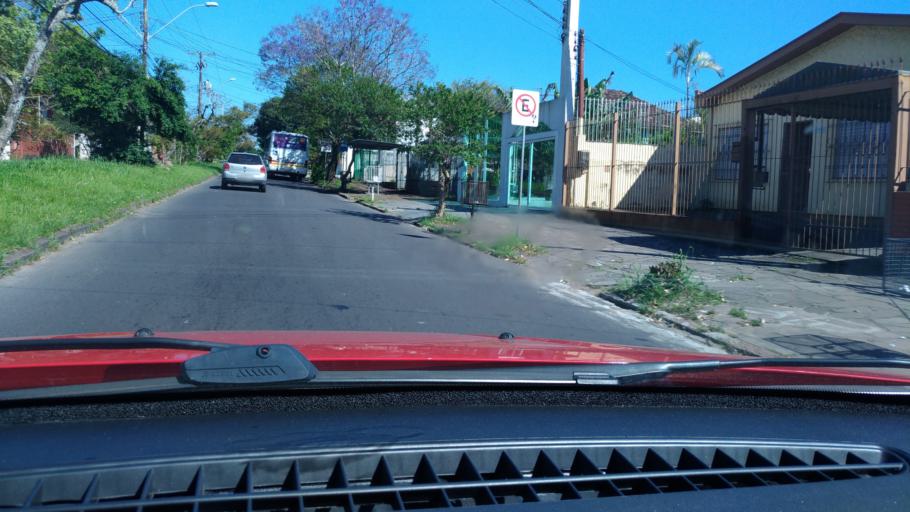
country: BR
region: Rio Grande do Sul
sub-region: Cachoeirinha
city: Cachoeirinha
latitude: -30.0312
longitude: -51.1364
